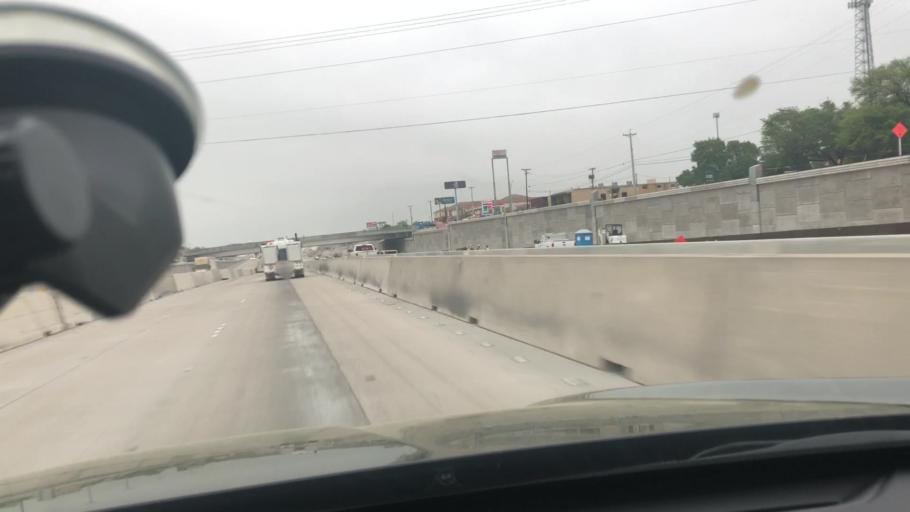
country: US
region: Texas
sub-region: Bell County
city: Temple
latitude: 31.1120
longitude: -97.3562
